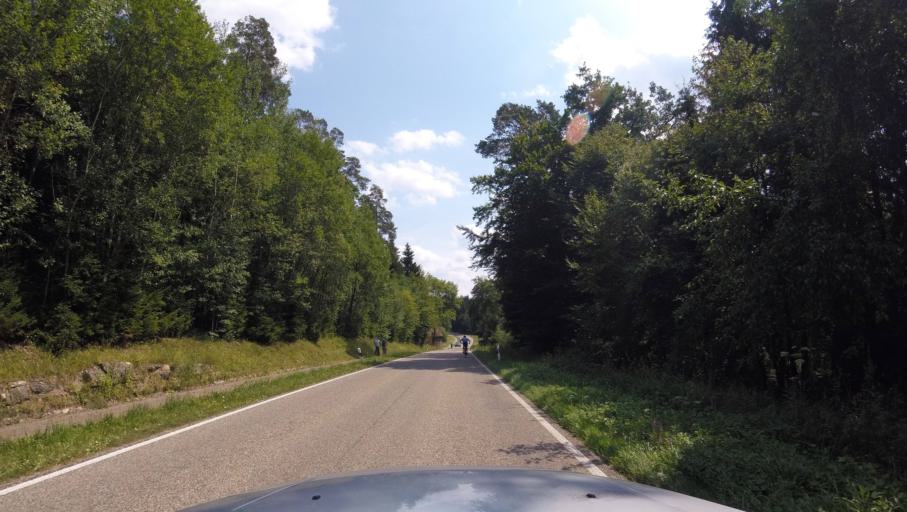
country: DE
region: Baden-Wuerttemberg
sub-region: Regierungsbezirk Stuttgart
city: Kaisersbach
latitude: 48.9140
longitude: 9.6726
